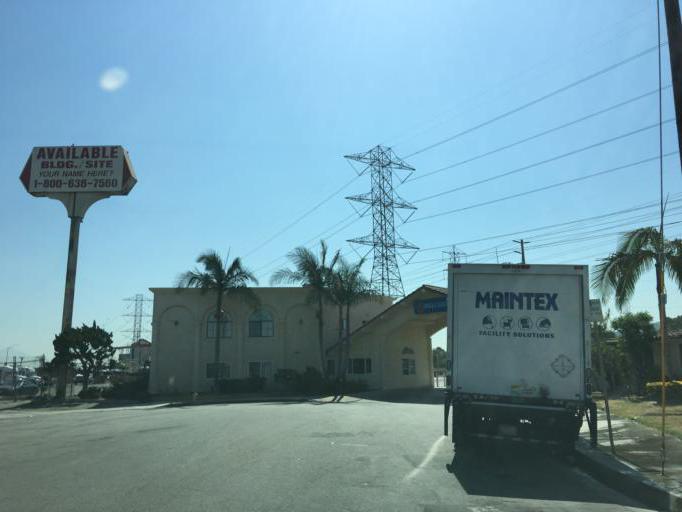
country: US
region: California
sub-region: Los Angeles County
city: South El Monte
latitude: 34.0362
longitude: -118.0379
